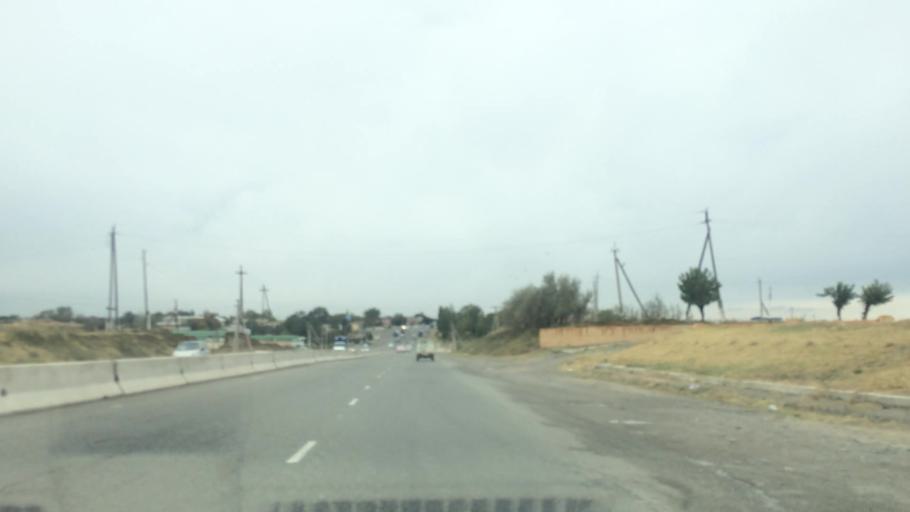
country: UZ
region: Samarqand
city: Bulung'ur
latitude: 39.7743
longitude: 67.2824
